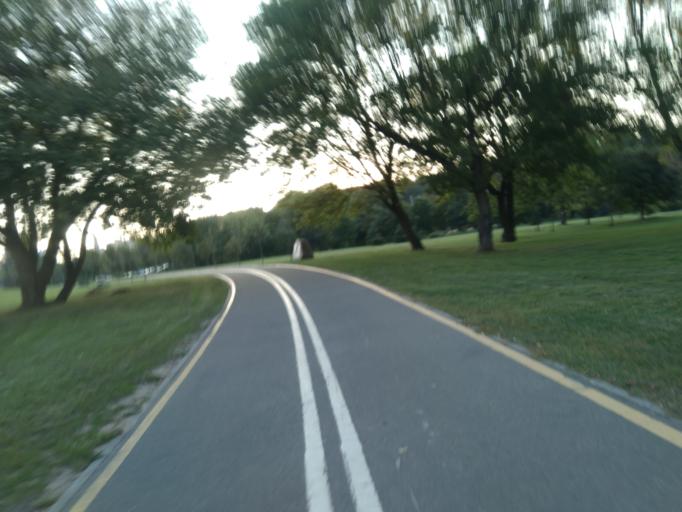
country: BY
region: Minsk
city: Minsk
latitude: 53.9178
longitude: 27.5465
